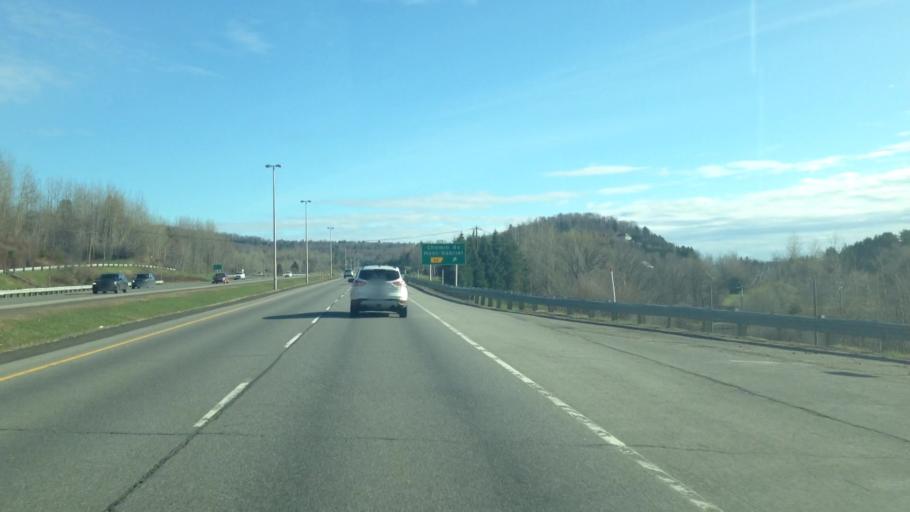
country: CA
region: Quebec
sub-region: Laurentides
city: Sainte-Adele
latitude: 45.9163
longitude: -74.1498
